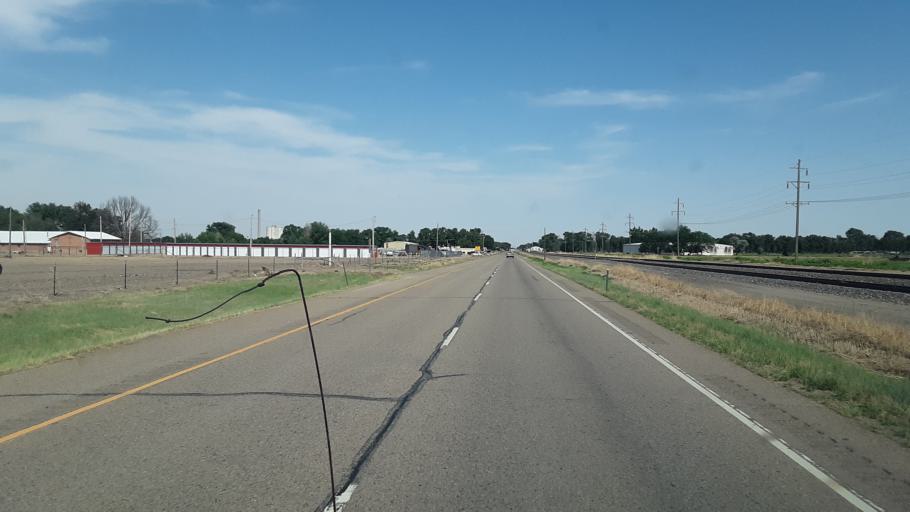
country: US
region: Colorado
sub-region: Otero County
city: Rocky Ford
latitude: 38.0616
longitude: -103.7414
